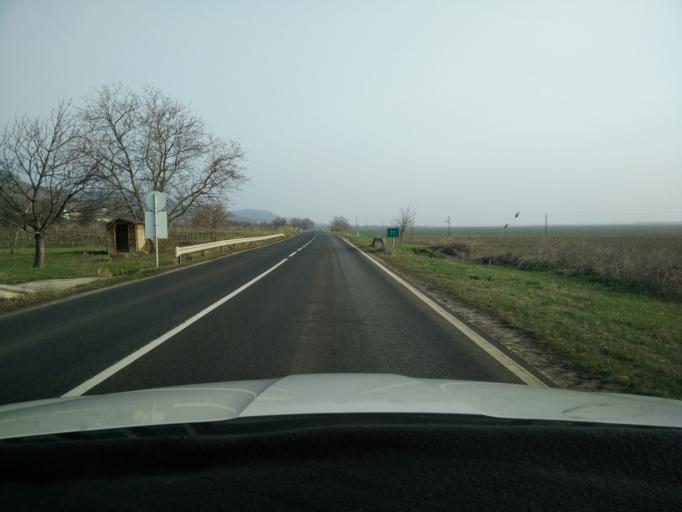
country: HU
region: Tolna
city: Szekszard
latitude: 46.2853
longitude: 18.6848
